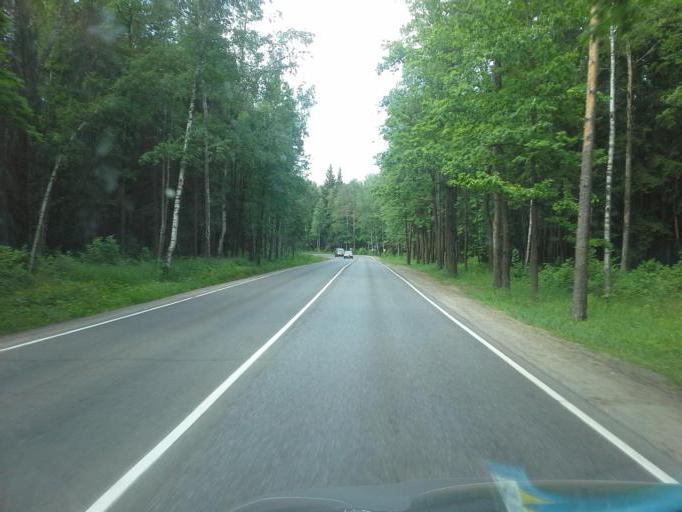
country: RU
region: Moskovskaya
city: Odintsovo
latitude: 55.7059
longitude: 37.2235
